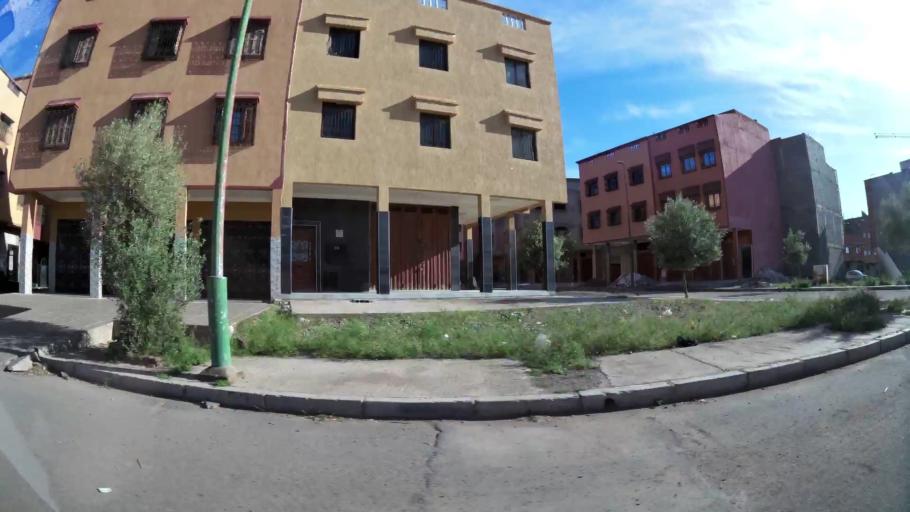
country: MA
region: Marrakech-Tensift-Al Haouz
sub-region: Marrakech
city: Marrakesh
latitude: 31.6901
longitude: -8.0664
